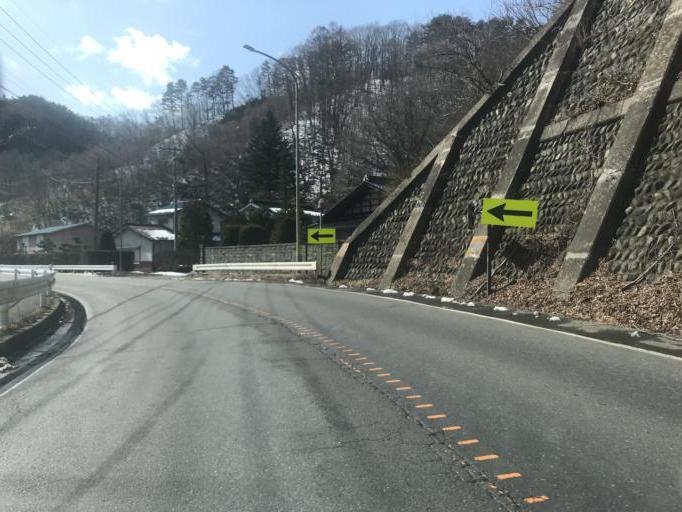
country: JP
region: Nagano
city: Saku
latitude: 36.0142
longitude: 138.4903
